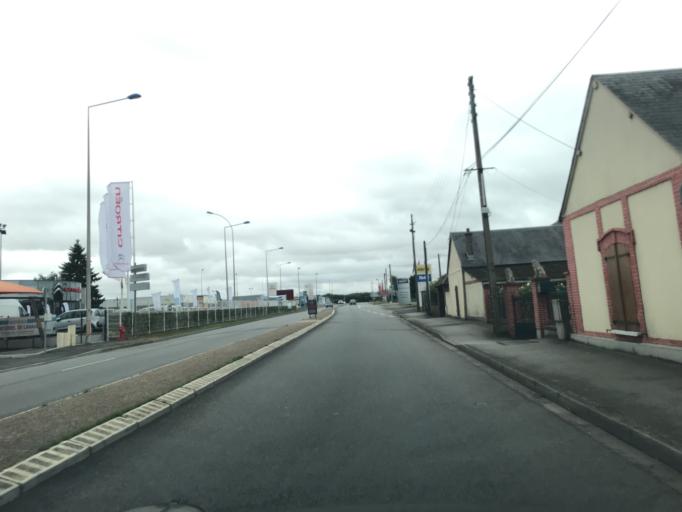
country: FR
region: Haute-Normandie
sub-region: Departement de l'Eure
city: Evreux
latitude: 49.0026
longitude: 1.1524
